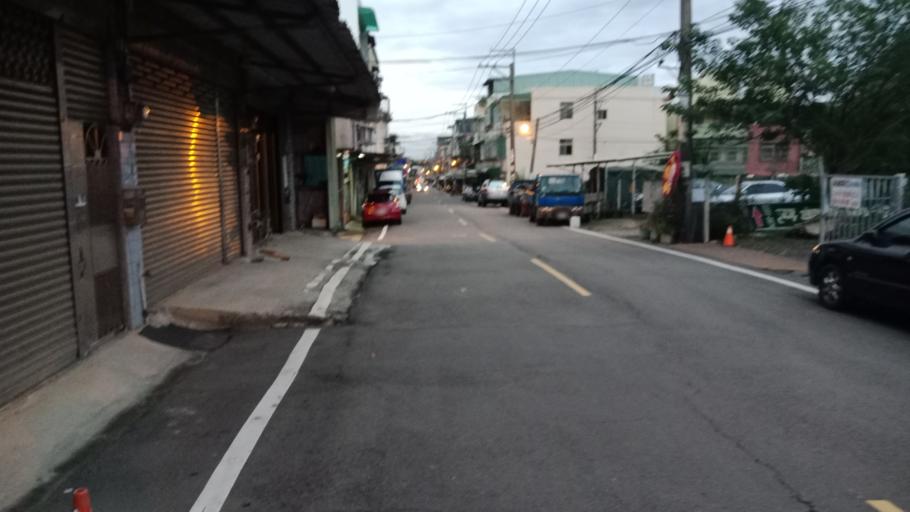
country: TW
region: Taiwan
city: Daxi
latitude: 24.8702
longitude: 121.1977
